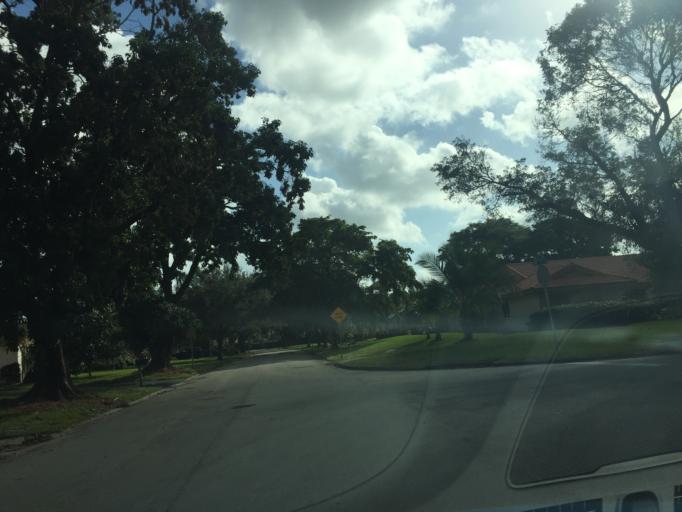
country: US
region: Florida
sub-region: Broward County
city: North Lauderdale
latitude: 26.2315
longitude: -80.2406
